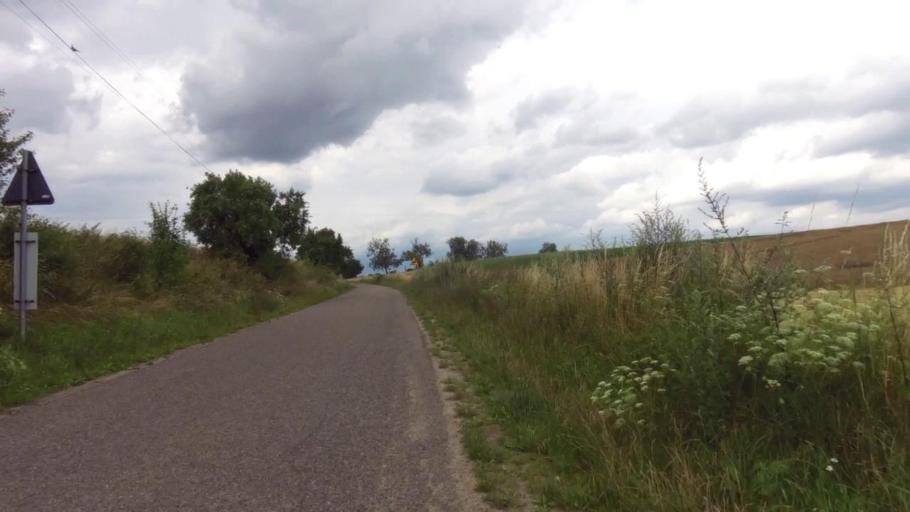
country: PL
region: West Pomeranian Voivodeship
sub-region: Powiat gryfinski
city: Moryn
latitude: 52.8743
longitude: 14.3910
